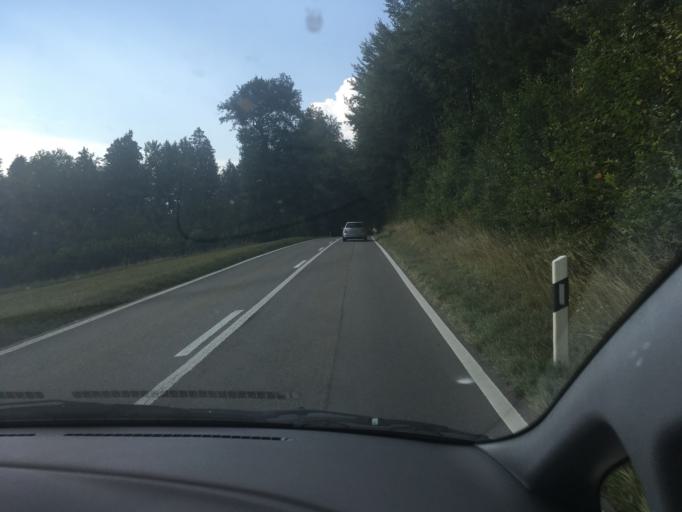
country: CH
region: Bern
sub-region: Bern-Mittelland District
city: Kirchlindach
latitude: 47.0029
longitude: 7.3852
